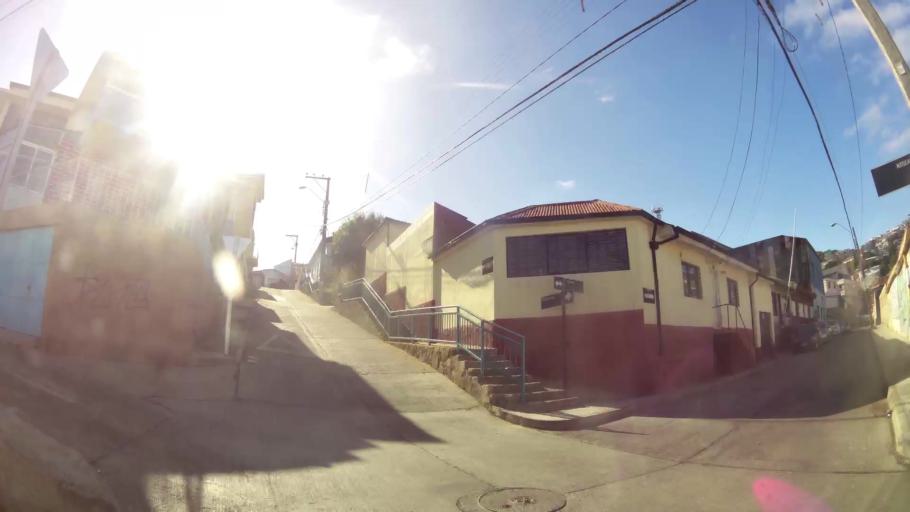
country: CL
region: Valparaiso
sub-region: Provincia de Valparaiso
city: Valparaiso
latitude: -33.0525
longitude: -71.6056
